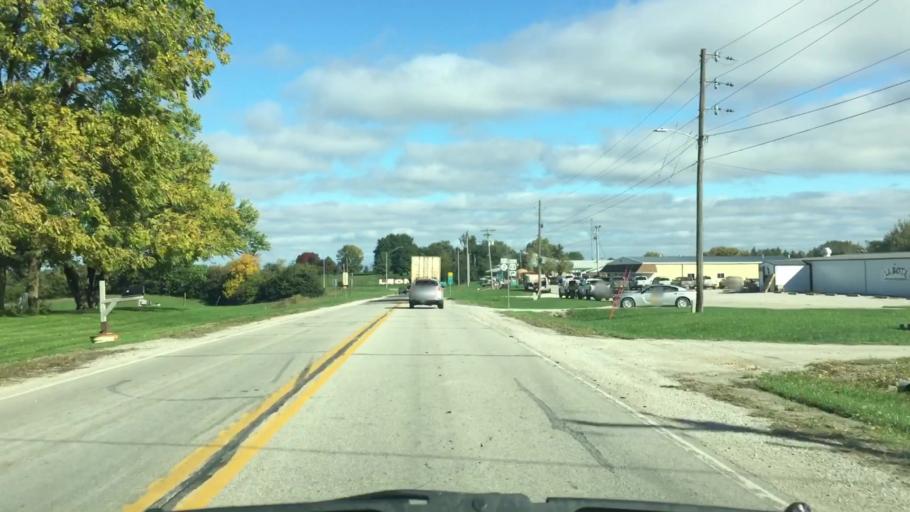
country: US
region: Iowa
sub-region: Decatur County
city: Leon
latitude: 40.7367
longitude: -93.7611
